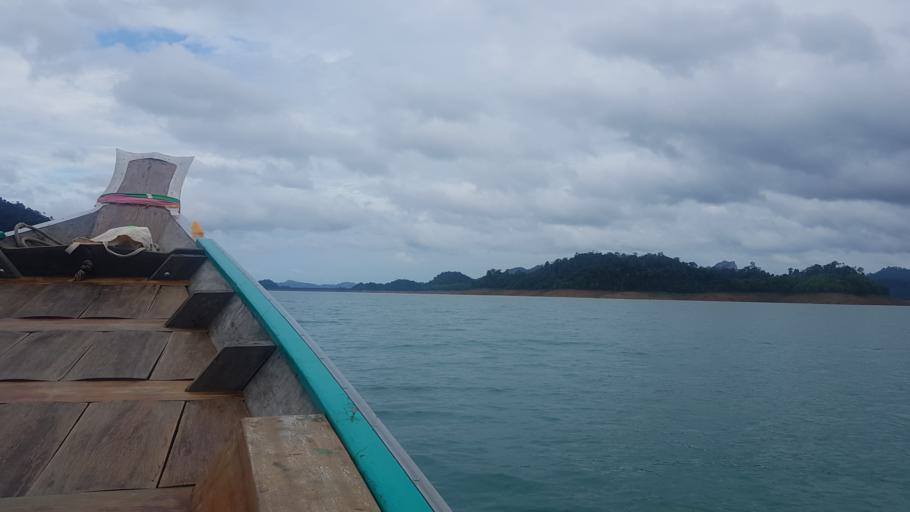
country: TH
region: Surat Thani
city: Ban Takhun
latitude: 9.0027
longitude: 98.7655
